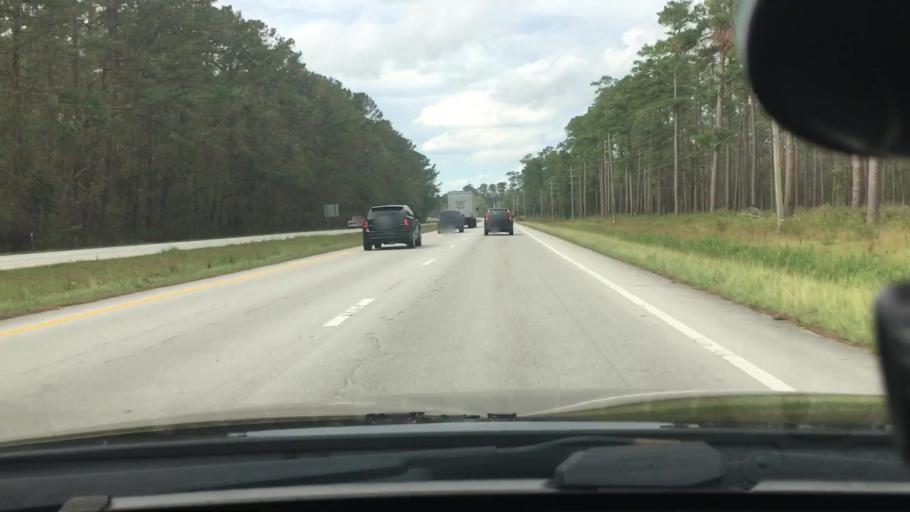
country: US
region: North Carolina
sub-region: Craven County
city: Neuse Forest
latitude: 34.9920
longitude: -76.9830
